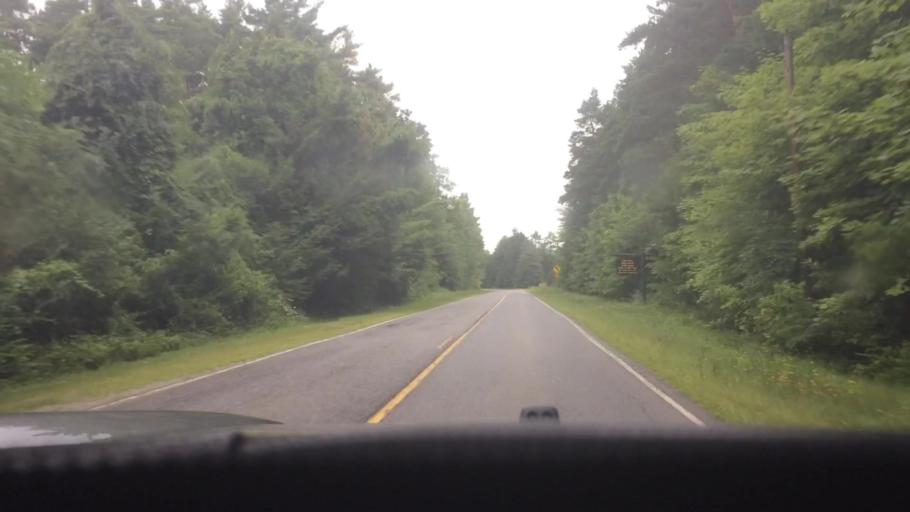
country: US
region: New York
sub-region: St. Lawrence County
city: Hannawa Falls
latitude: 44.6002
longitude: -74.8858
